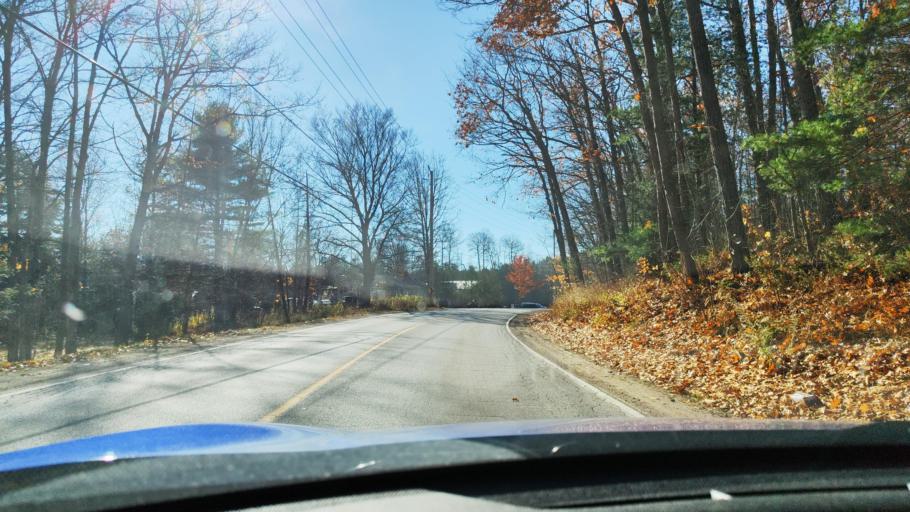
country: CA
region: Ontario
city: Wasaga Beach
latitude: 44.4889
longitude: -80.0057
